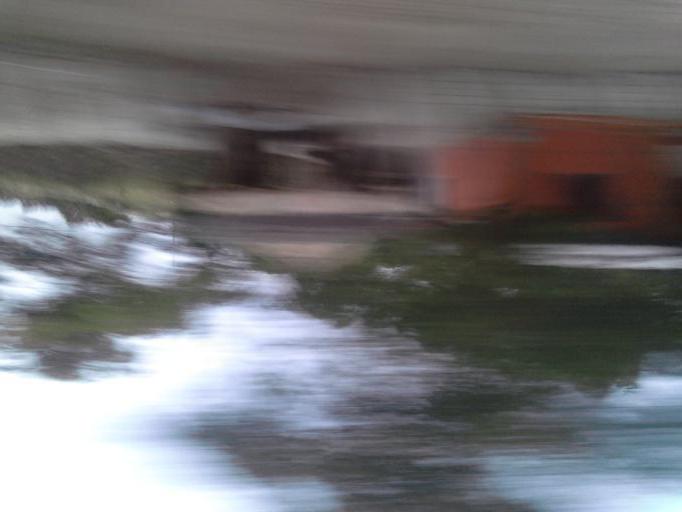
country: CO
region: Sucre
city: Morroa
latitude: 9.3532
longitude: -75.2852
